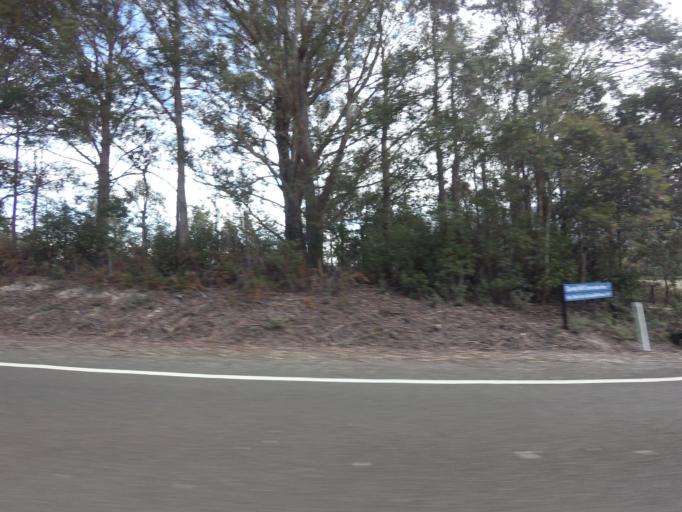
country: AU
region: Tasmania
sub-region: Meander Valley
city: Deloraine
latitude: -41.6596
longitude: 146.7230
